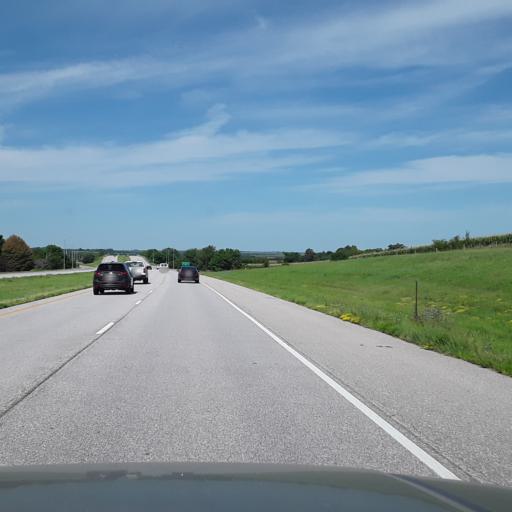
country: US
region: Nebraska
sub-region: Lancaster County
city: Lincoln
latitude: 40.8794
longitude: -96.7498
